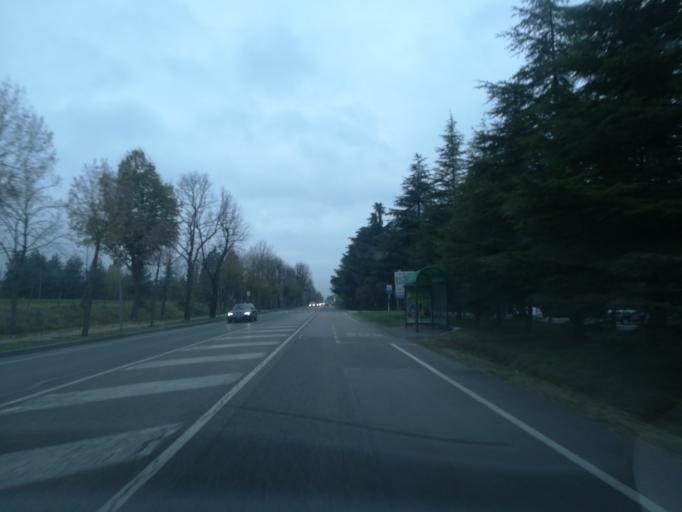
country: IT
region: Emilia-Romagna
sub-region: Provincia di Bologna
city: Imola
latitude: 44.3647
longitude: 11.6854
